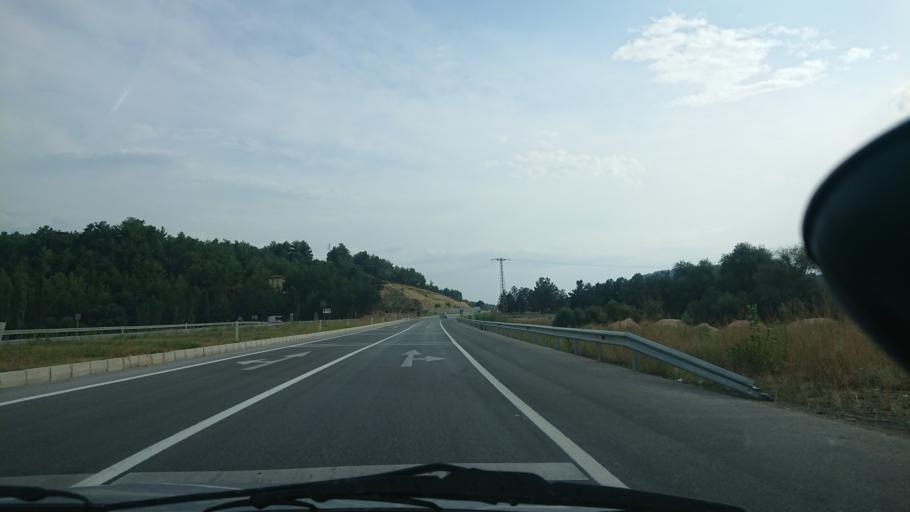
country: TR
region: Kuetahya
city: Gediz
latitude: 38.9271
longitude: 29.3049
